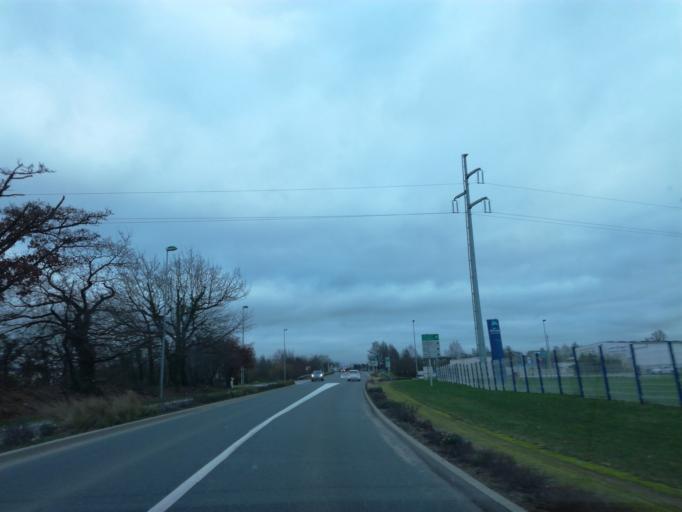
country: FR
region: Brittany
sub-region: Departement du Morbihan
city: Saint-Thuriau
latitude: 48.0416
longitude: -2.9540
